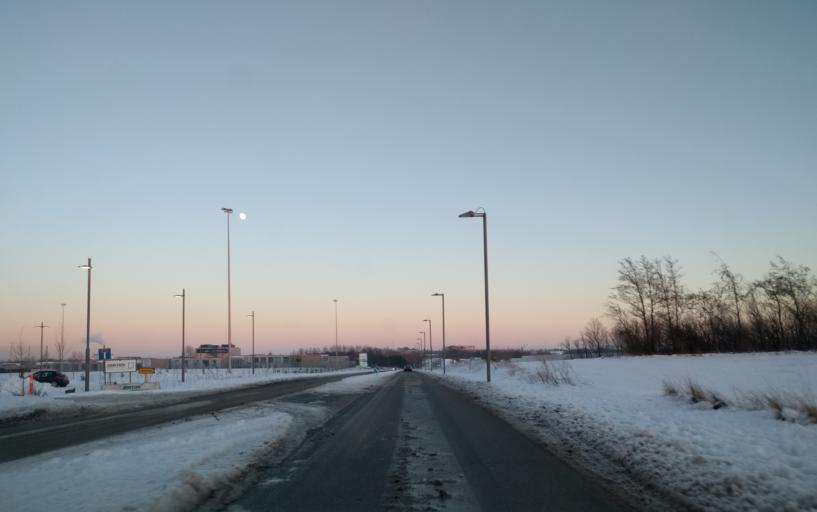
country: DK
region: North Denmark
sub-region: Alborg Kommune
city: Gistrup
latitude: 57.0127
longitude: 9.9718
